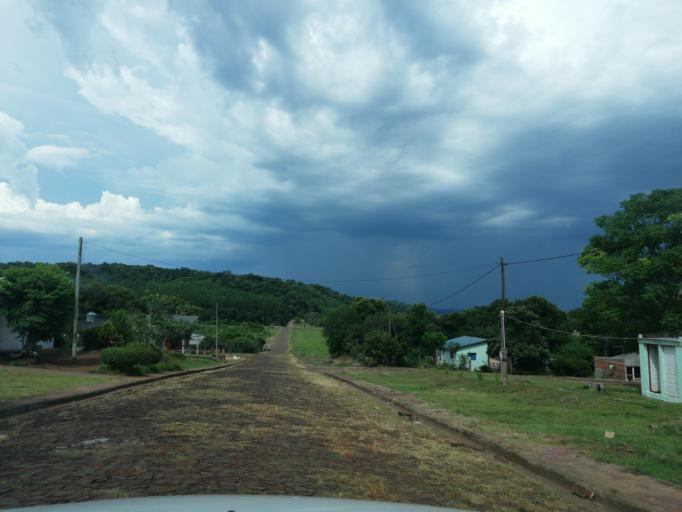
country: AR
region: Misiones
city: Cerro Azul
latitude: -27.5729
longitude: -55.5009
